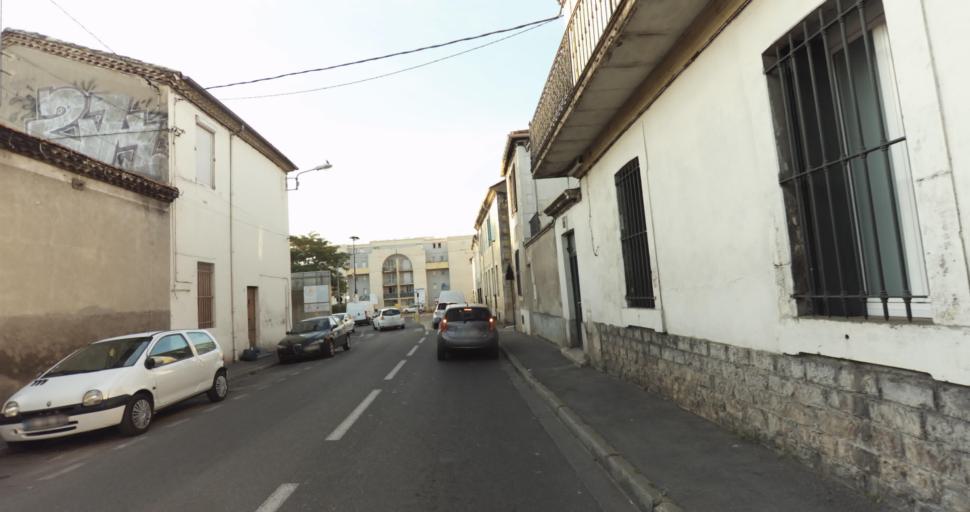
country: FR
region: Languedoc-Roussillon
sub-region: Departement du Gard
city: Nimes
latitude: 43.8412
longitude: 4.3717
